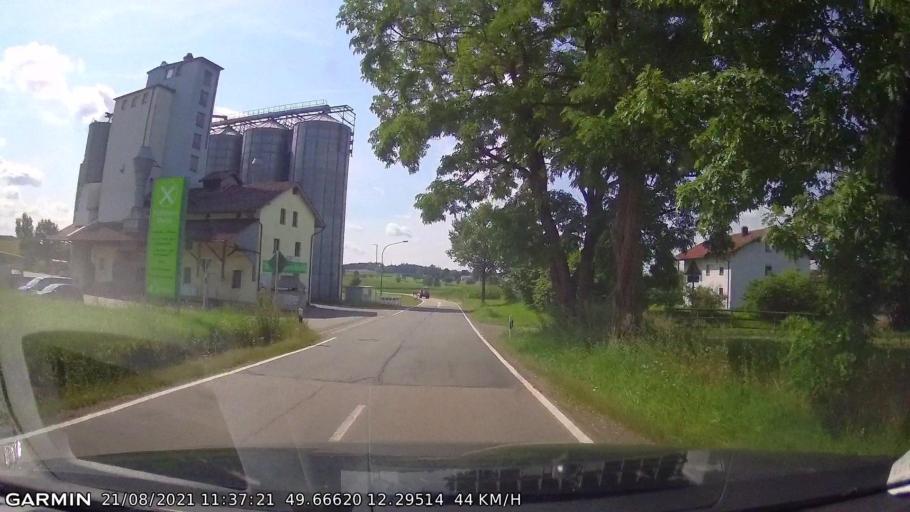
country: DE
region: Bavaria
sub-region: Upper Palatinate
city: Waldthurn
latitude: 49.6662
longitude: 12.2951
